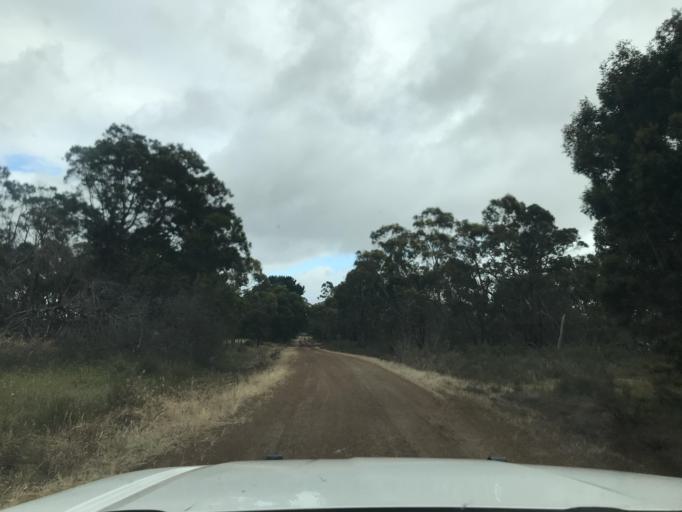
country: AU
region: South Australia
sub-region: Wattle Range
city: Penola
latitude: -37.2494
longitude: 141.3576
